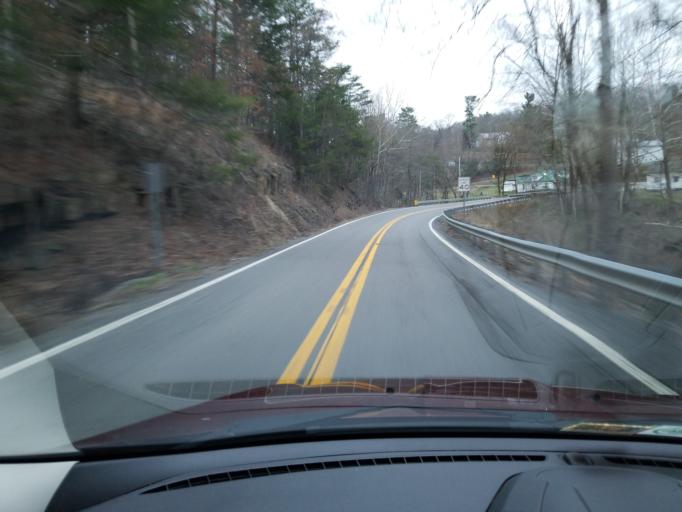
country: US
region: West Virginia
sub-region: Monroe County
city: Union
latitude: 37.4990
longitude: -80.6086
